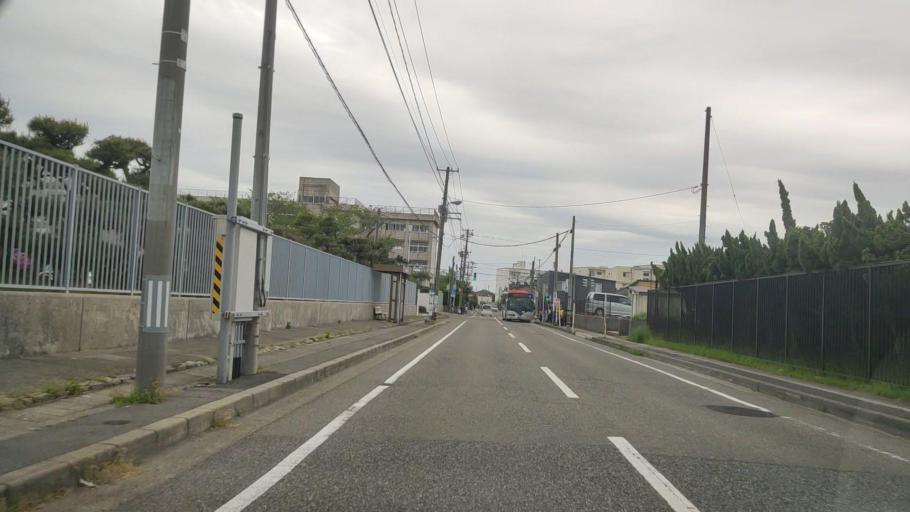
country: JP
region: Niigata
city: Niigata-shi
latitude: 37.9454
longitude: 139.0774
